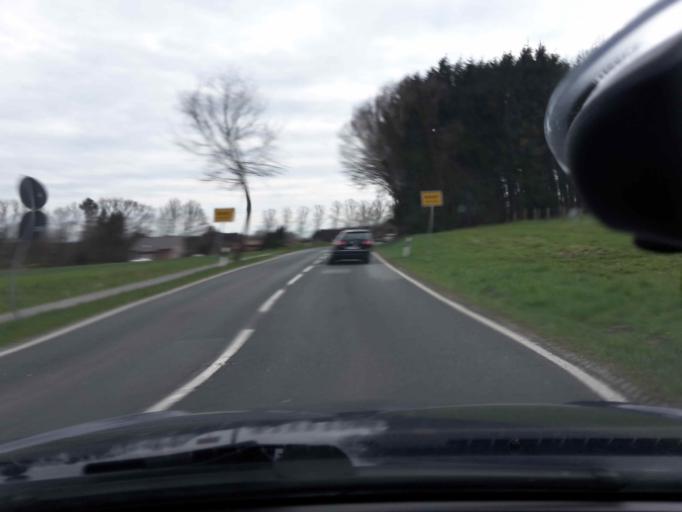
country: DE
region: Lower Saxony
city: Harmstorf
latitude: 53.3530
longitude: 9.9914
